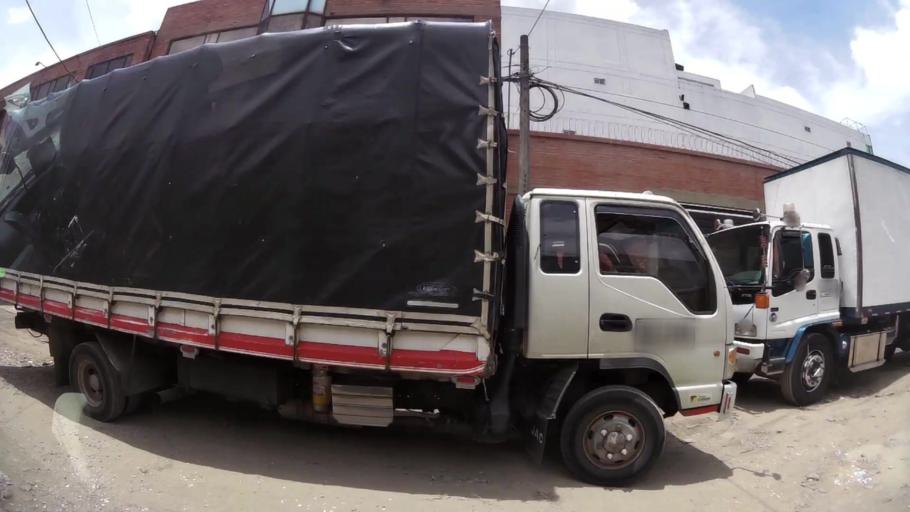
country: CO
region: Bogota D.C.
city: Bogota
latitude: 4.6477
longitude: -74.1478
